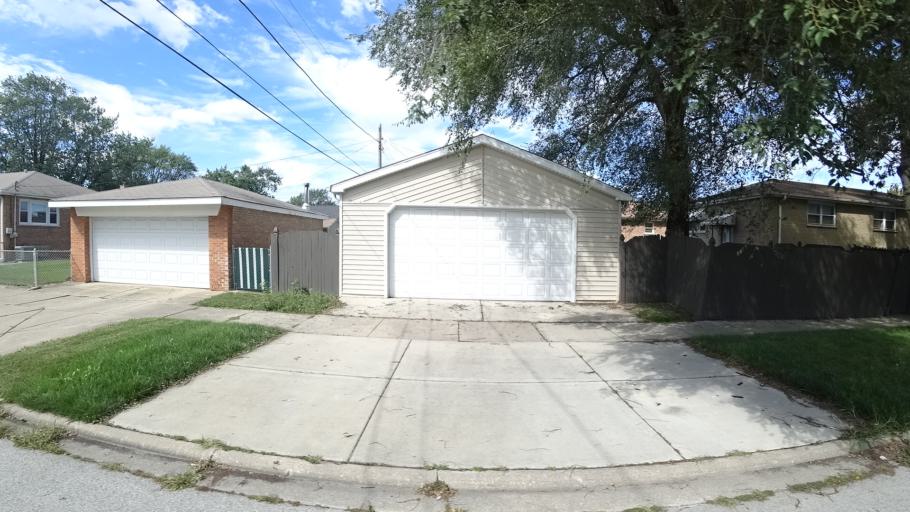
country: US
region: Illinois
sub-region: Cook County
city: Oak Lawn
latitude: 41.7216
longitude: -87.7622
